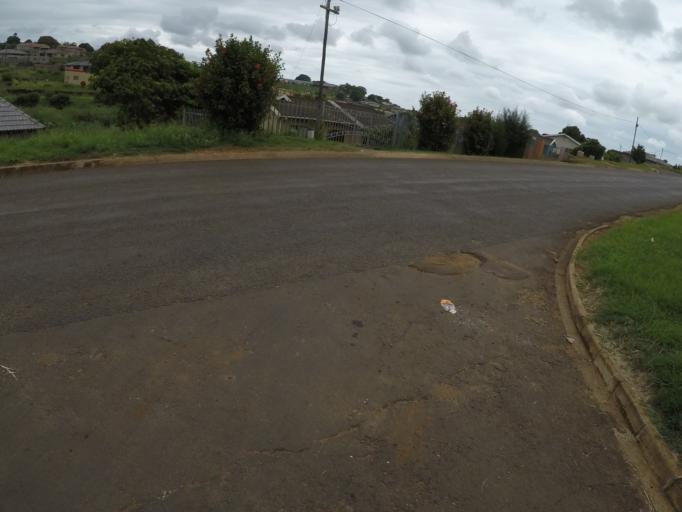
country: ZA
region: KwaZulu-Natal
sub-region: uThungulu District Municipality
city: Empangeni
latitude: -28.7797
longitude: 31.8582
